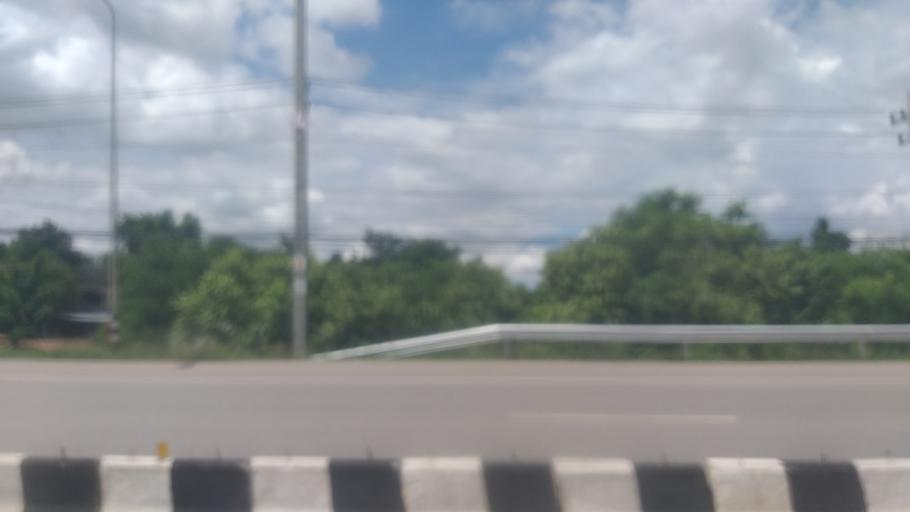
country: TH
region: Nakhon Ratchasima
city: Non Thai
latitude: 15.1418
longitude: 102.1046
